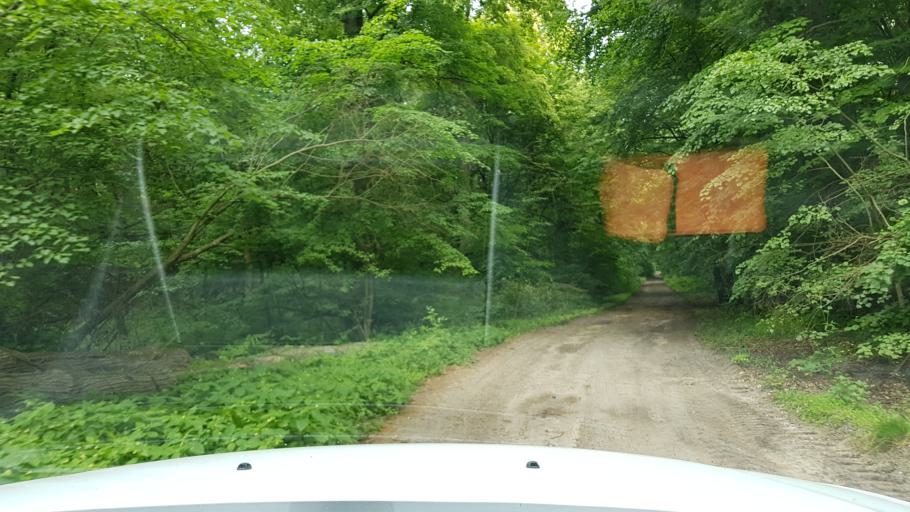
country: PL
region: West Pomeranian Voivodeship
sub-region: Powiat mysliborski
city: Boleszkowice
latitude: 52.6684
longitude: 14.5846
